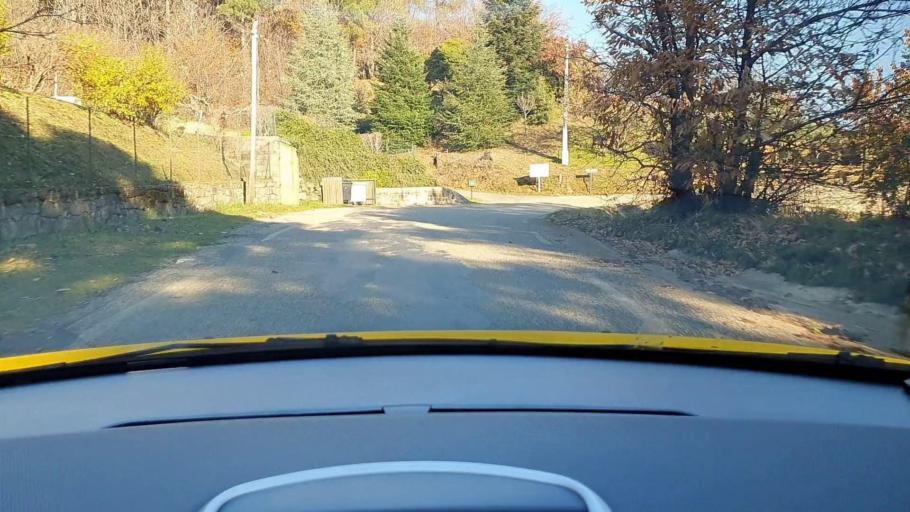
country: FR
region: Languedoc-Roussillon
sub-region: Departement du Gard
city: Branoux-les-Taillades
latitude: 44.2193
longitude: 3.9824
